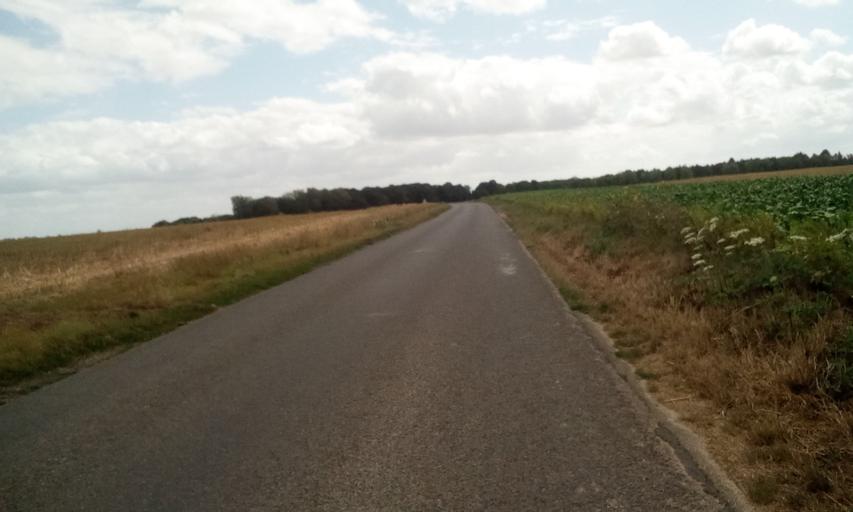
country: FR
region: Lower Normandy
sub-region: Departement du Calvados
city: Creully
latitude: 49.2764
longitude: -0.5316
